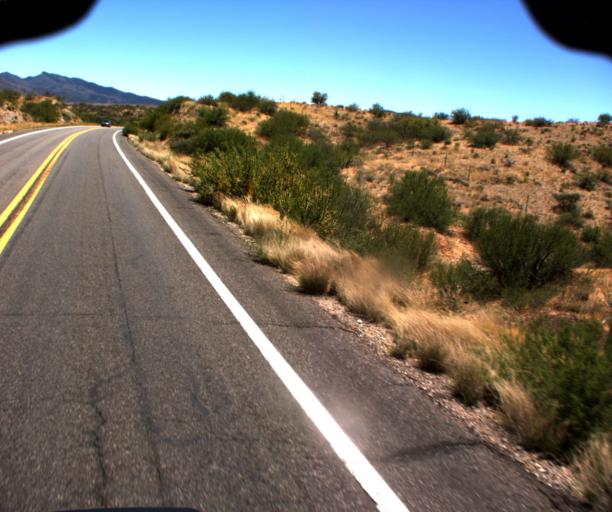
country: US
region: Arizona
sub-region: Gila County
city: Globe
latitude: 33.3499
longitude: -110.7326
